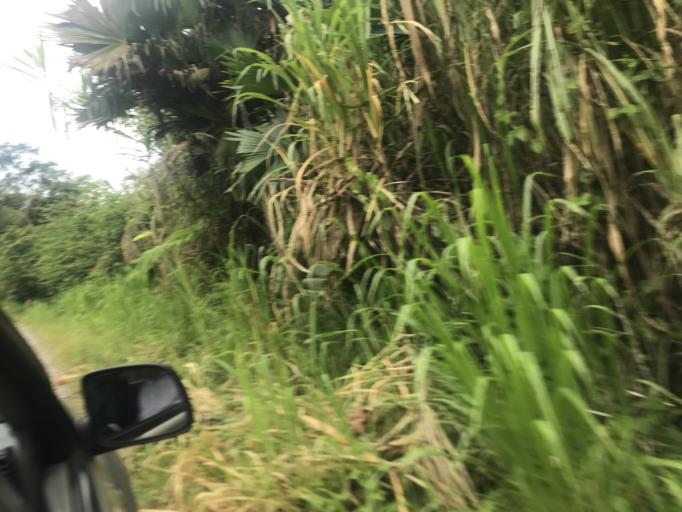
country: EC
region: Napo
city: Tena
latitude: -1.0241
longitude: -77.7420
